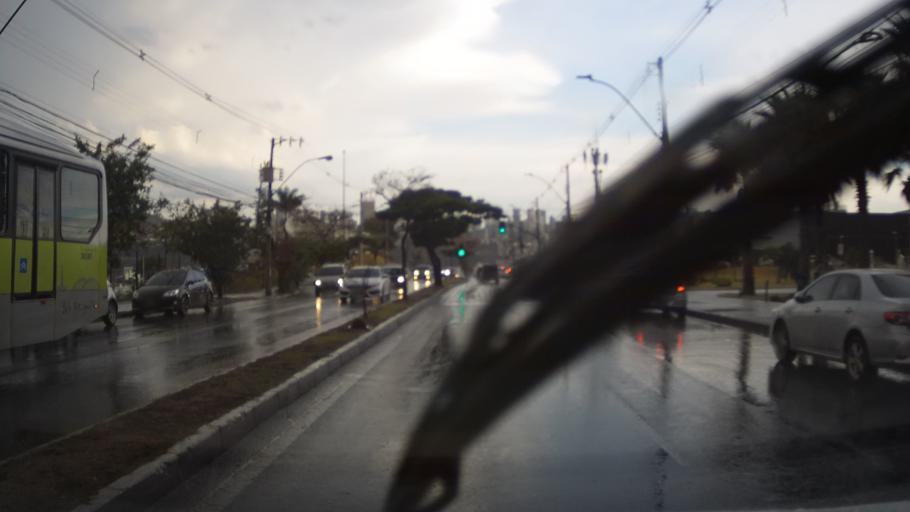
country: BR
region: Minas Gerais
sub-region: Belo Horizonte
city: Belo Horizonte
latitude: -19.9542
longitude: -43.9590
